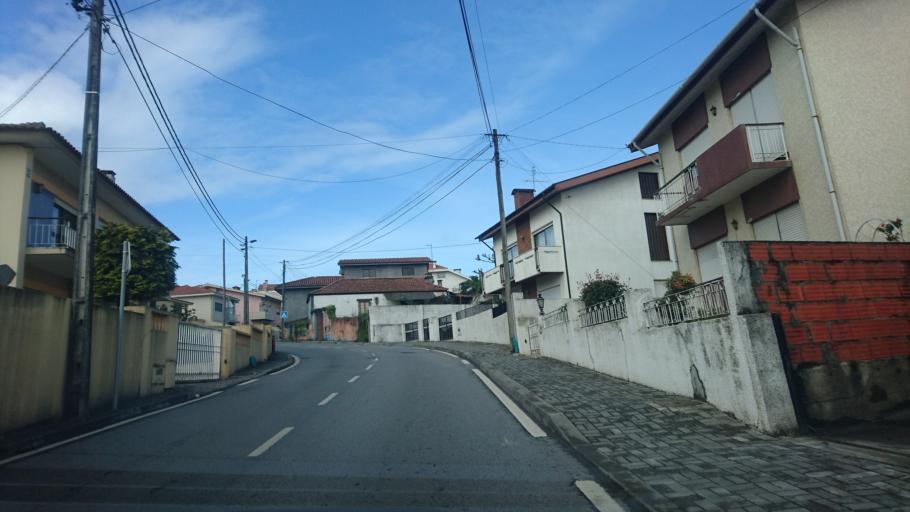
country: PT
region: Aveiro
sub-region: Espinho
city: Silvalde
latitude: 41.0059
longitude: -8.6221
